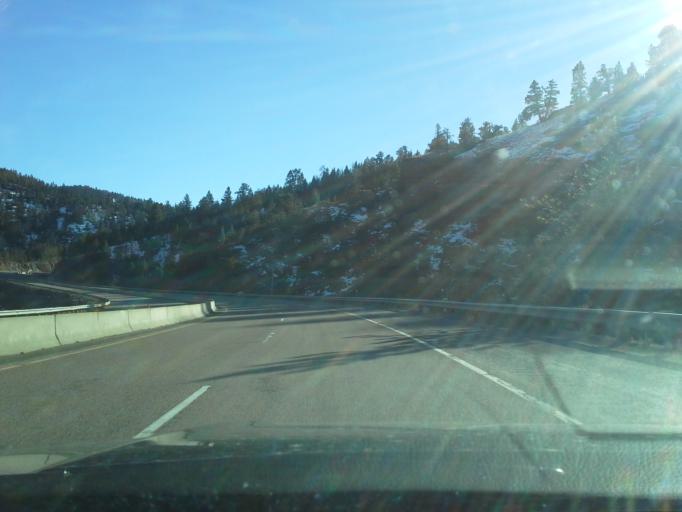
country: US
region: Montana
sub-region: Lewis and Clark County
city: Helena Valley Northwest
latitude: 46.9310
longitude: -112.1262
